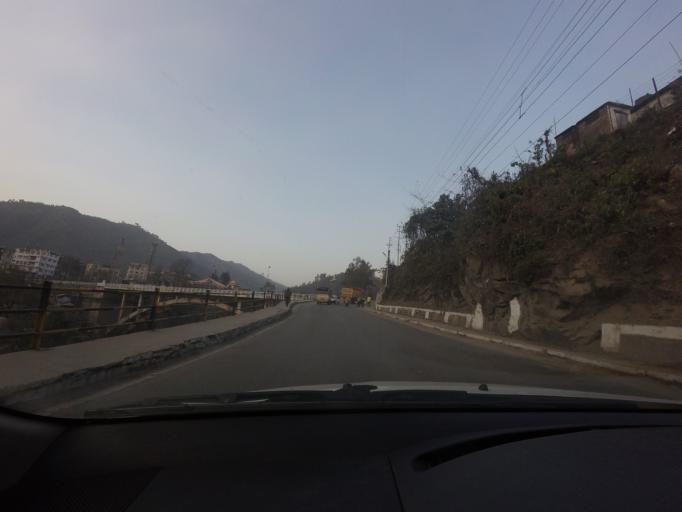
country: IN
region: Himachal Pradesh
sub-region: Mandi
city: Mandi
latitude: 31.7058
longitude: 76.9350
